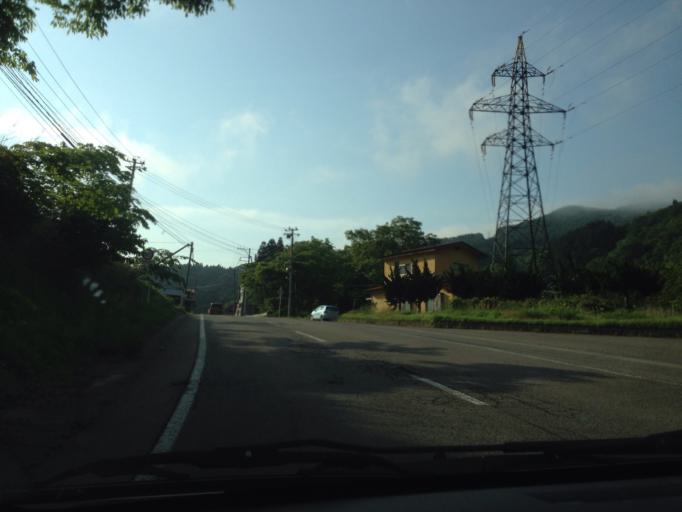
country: JP
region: Fukushima
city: Inawashiro
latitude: 37.3042
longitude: 139.9274
